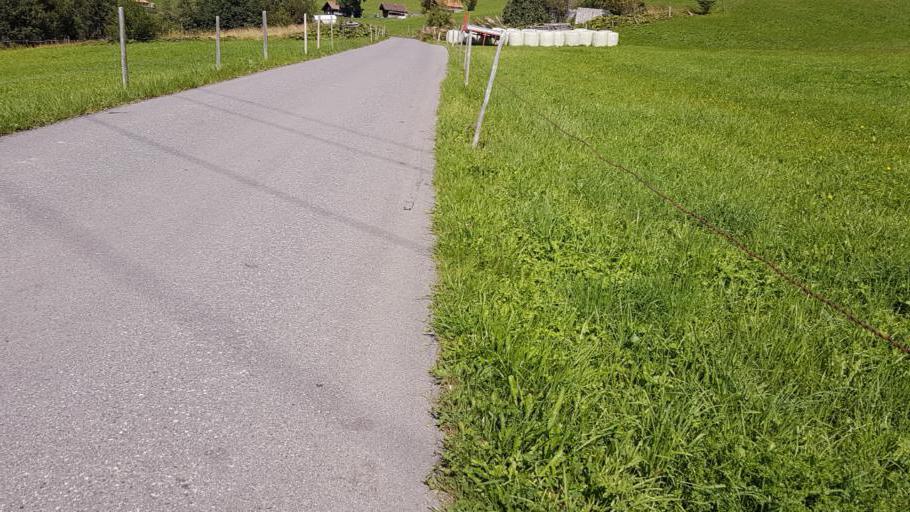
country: CH
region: Bern
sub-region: Frutigen-Niedersimmental District
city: Frutigen
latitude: 46.5370
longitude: 7.6110
